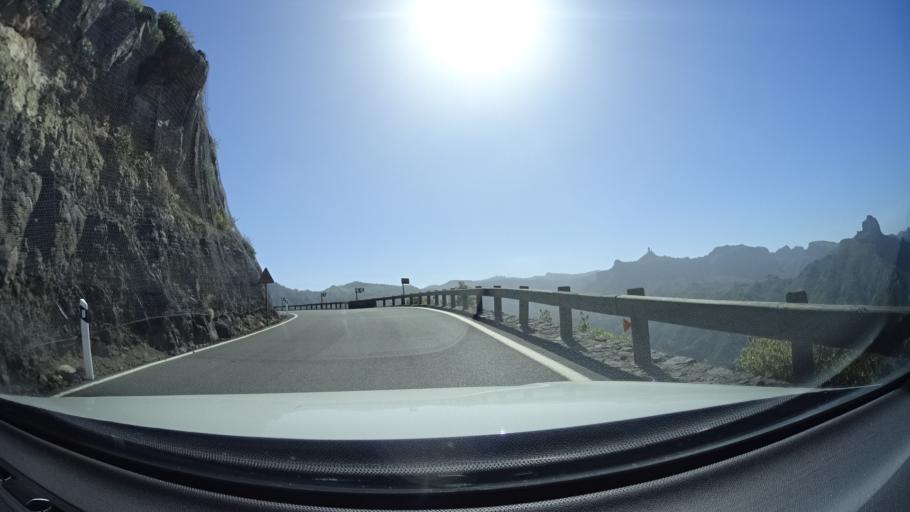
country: ES
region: Canary Islands
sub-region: Provincia de Las Palmas
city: Artenara
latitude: 28.0161
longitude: -15.6380
